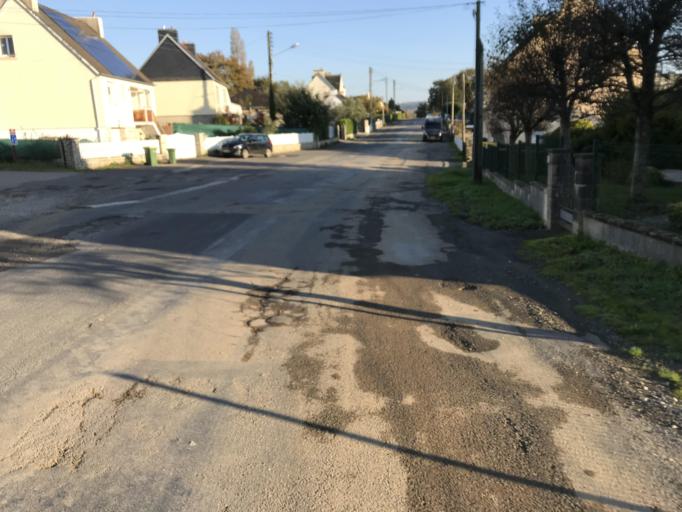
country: FR
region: Brittany
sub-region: Departement du Finistere
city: Le Faou
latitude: 48.2985
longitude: -4.1921
